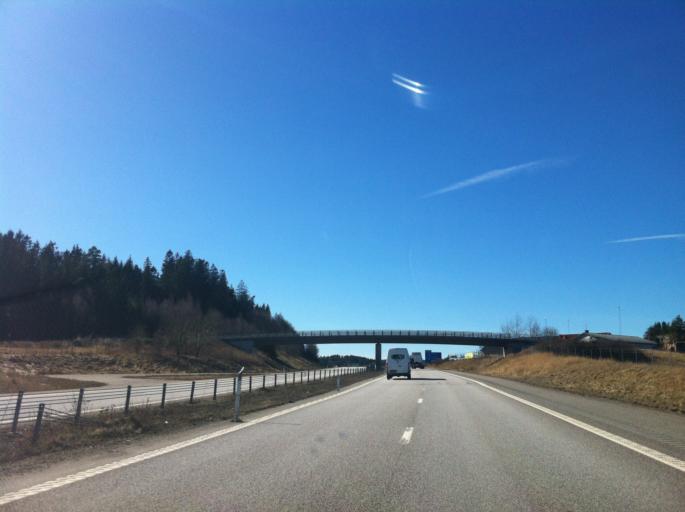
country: SE
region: Vaestra Goetaland
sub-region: Munkedals Kommun
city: Munkedal
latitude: 58.4081
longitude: 11.7364
